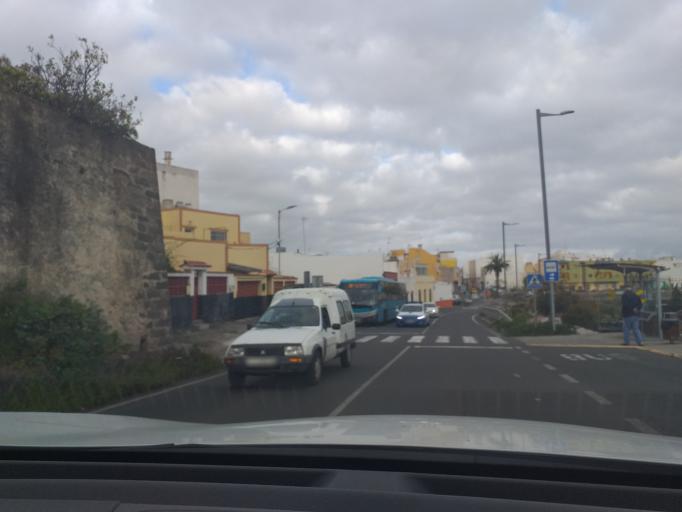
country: ES
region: Canary Islands
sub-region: Provincia de Las Palmas
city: Arucas
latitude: 28.1118
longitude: -15.5123
